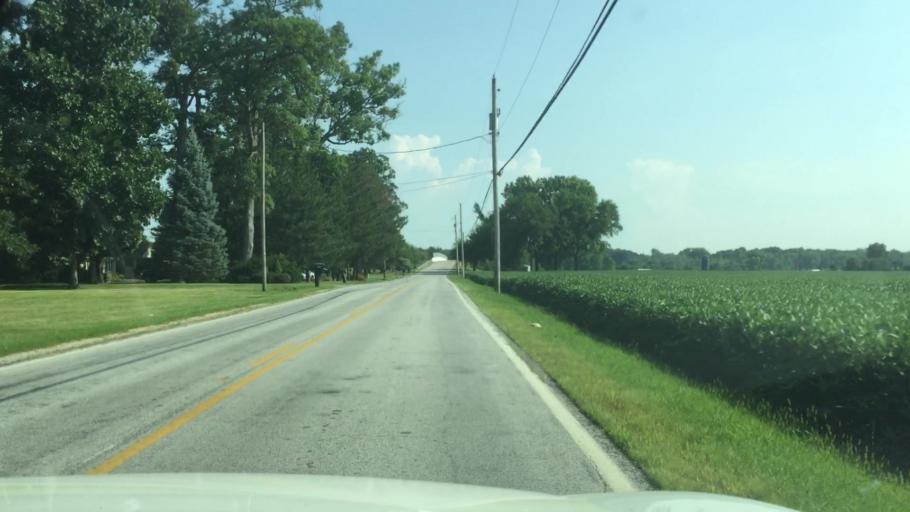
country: US
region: Ohio
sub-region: Clark County
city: Lisbon
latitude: 39.9322
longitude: -83.6824
